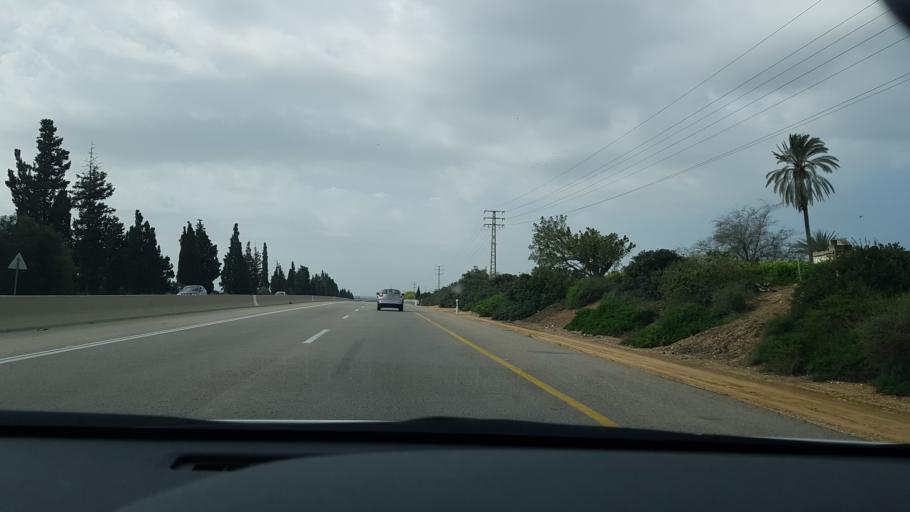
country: IL
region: Southern District
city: Ashqelon
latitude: 31.6363
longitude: 34.5900
